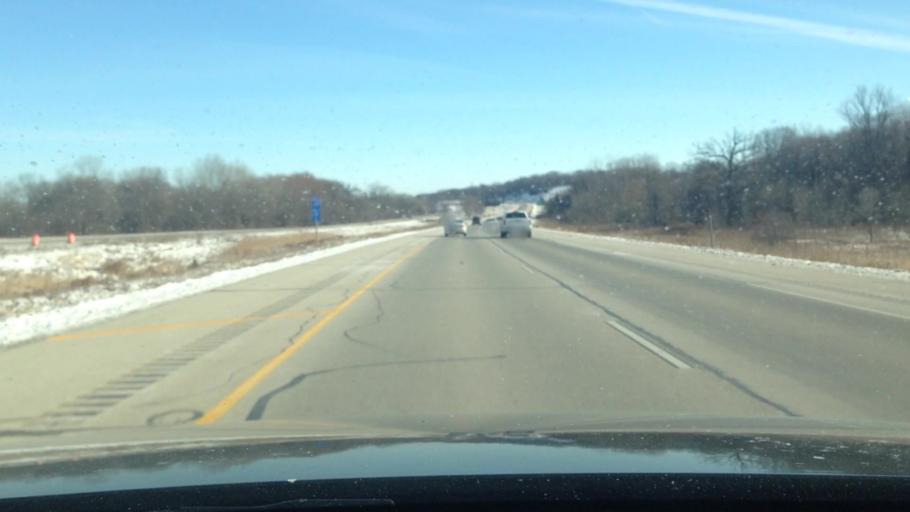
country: US
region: Wisconsin
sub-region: Waukesha County
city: Muskego
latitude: 42.9380
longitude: -88.1435
